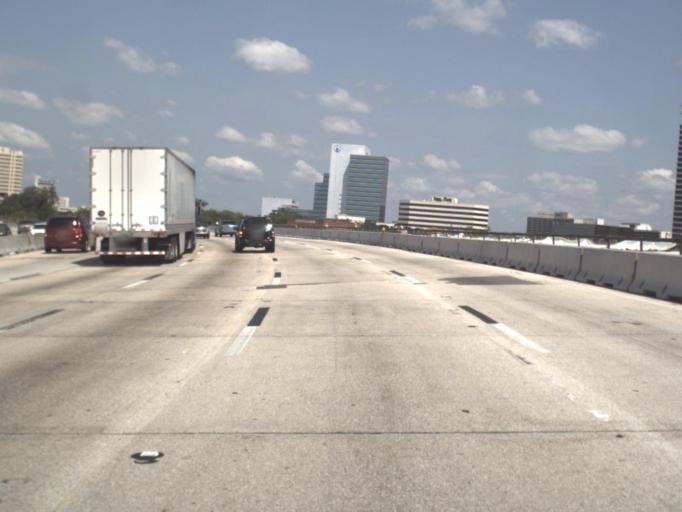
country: US
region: Florida
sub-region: Duval County
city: Jacksonville
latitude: 30.3136
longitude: -81.6520
